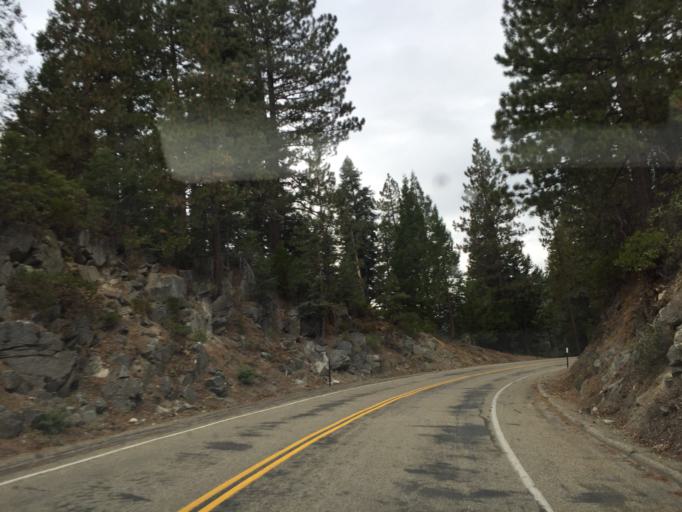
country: US
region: California
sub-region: Tulare County
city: Three Rivers
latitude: 36.7159
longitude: -118.9406
